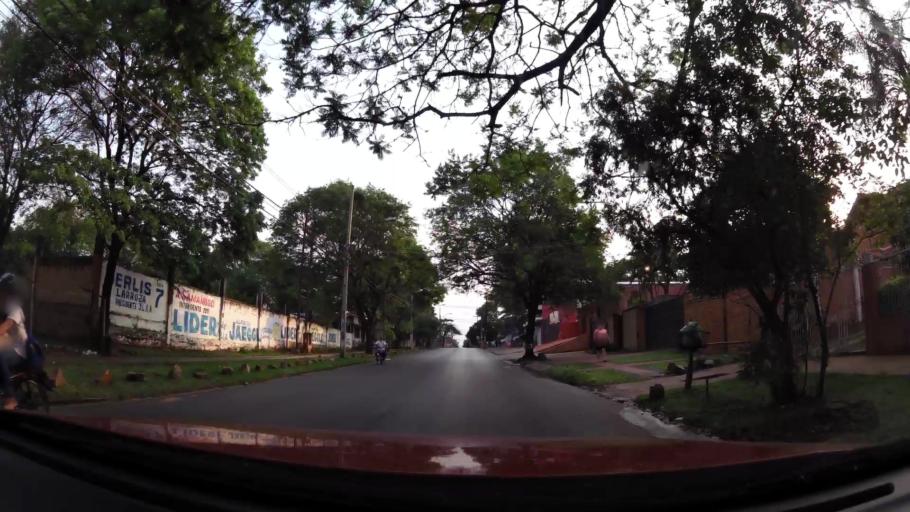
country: PY
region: Central
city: Lambare
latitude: -25.3226
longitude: -57.5795
